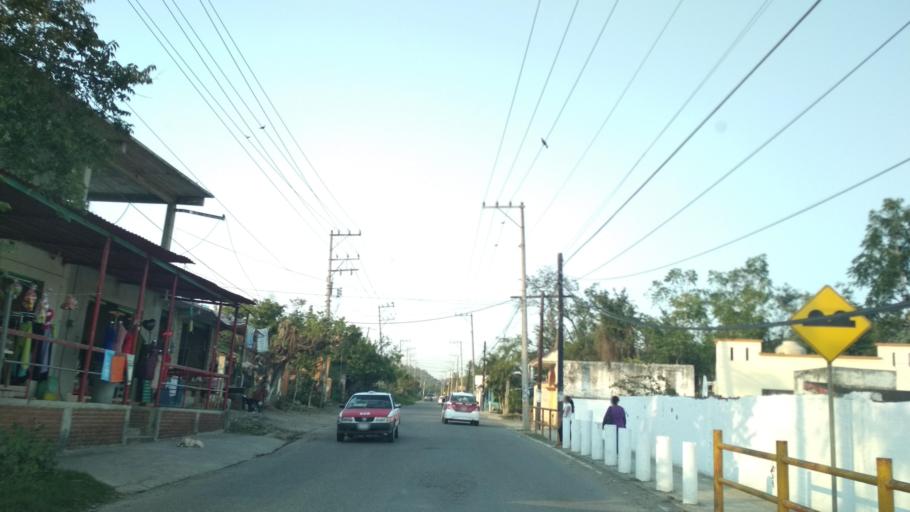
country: MM
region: Shan
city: Taunggyi
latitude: 20.4057
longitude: 97.3377
